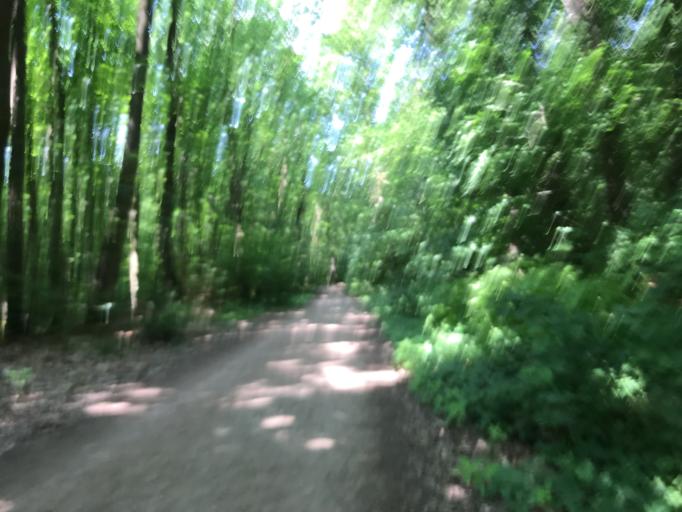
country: DE
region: Hesse
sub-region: Regierungsbezirk Darmstadt
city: Walluf
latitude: 50.0851
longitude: 8.1843
